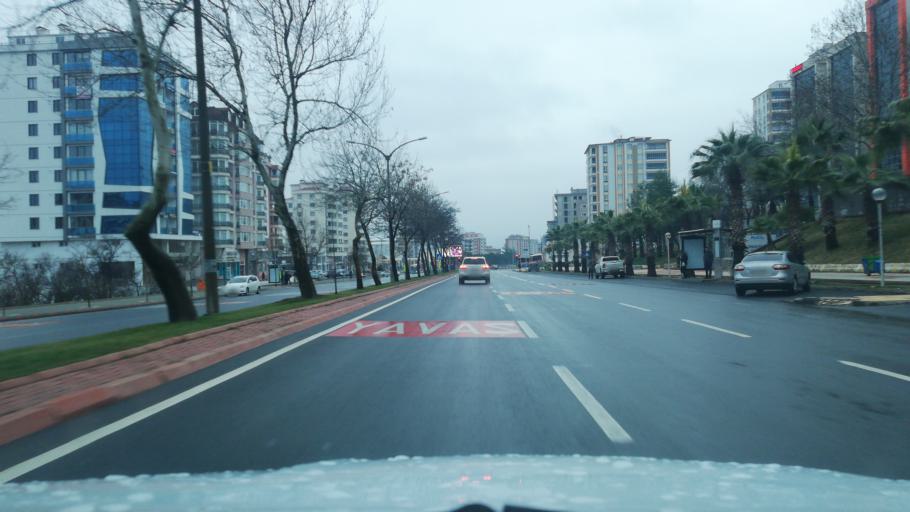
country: TR
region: Kahramanmaras
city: Kahramanmaras
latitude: 37.5929
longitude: 36.8617
